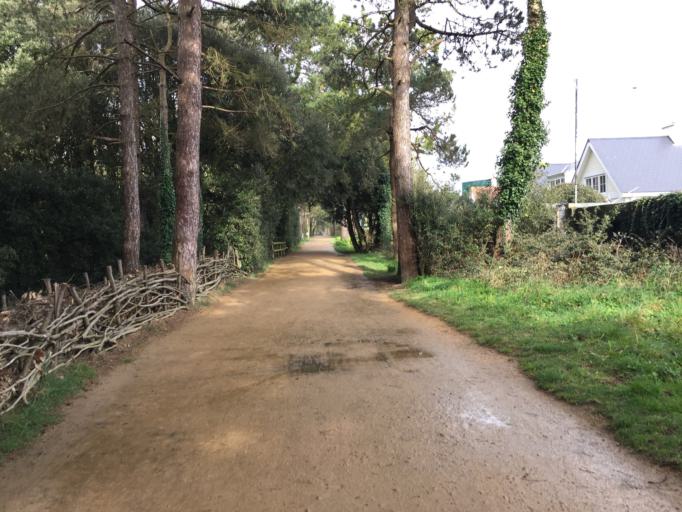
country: JE
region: St Helier
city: Saint Helier
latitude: 49.1926
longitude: -2.2092
